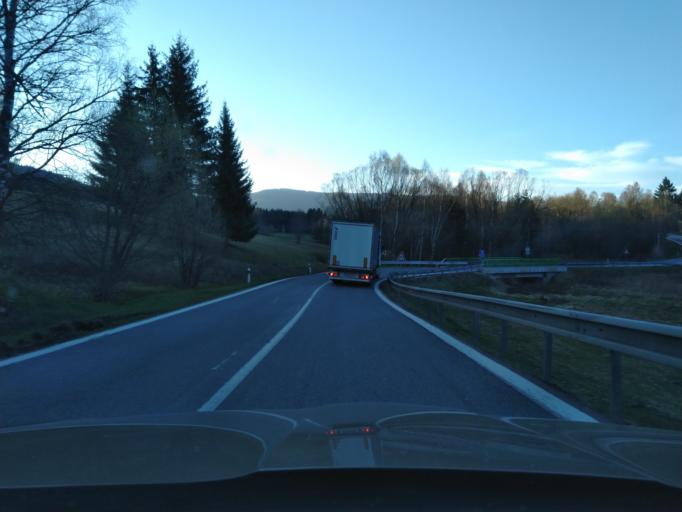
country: CZ
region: Jihocesky
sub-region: Okres Prachatice
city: Vimperk
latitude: 49.0259
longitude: 13.7662
